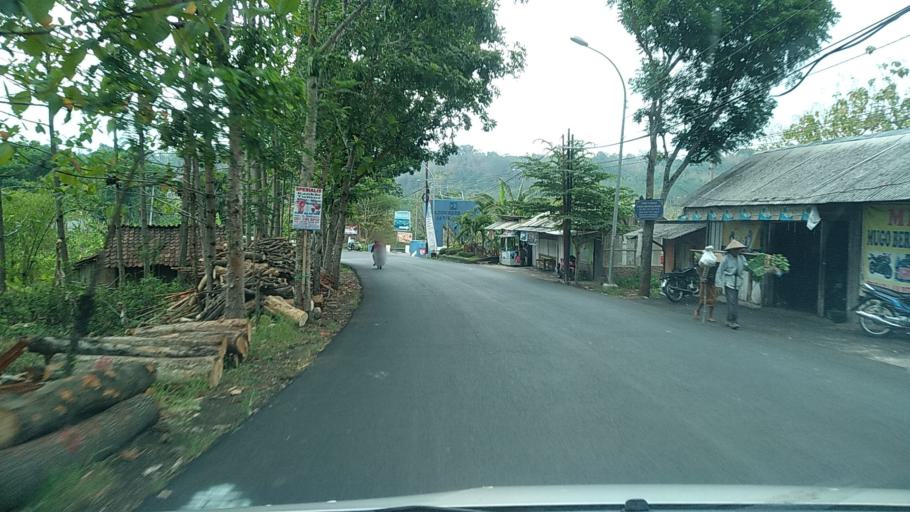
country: ID
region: Central Java
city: Semarang
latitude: -7.0415
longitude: 110.3607
